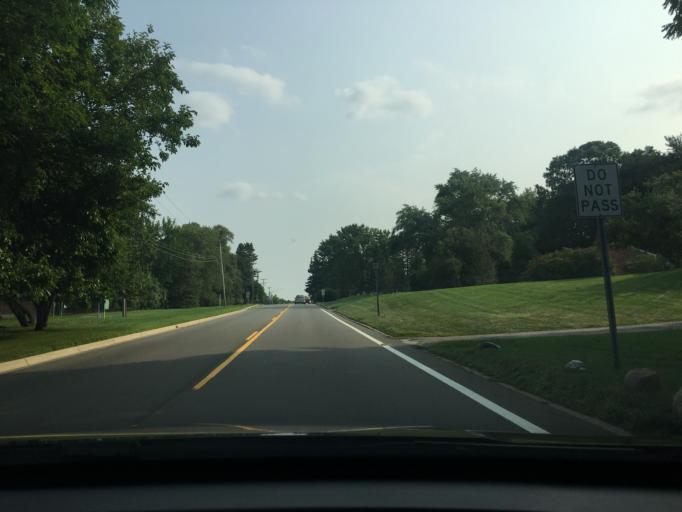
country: US
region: Michigan
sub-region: Oakland County
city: Bingham Farms
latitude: 42.5487
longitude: -83.2640
